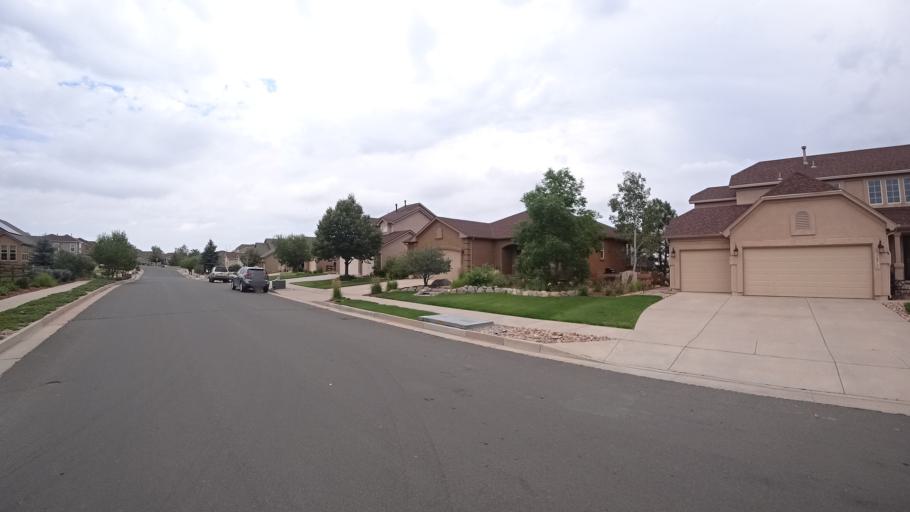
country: US
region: Colorado
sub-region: El Paso County
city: Gleneagle
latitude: 39.0024
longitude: -104.7921
